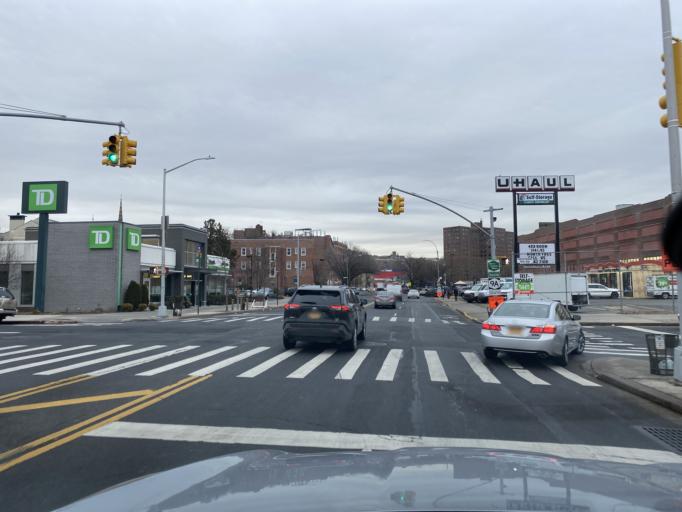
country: US
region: New York
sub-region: New York County
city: Inwood
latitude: 40.8796
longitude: -73.9099
